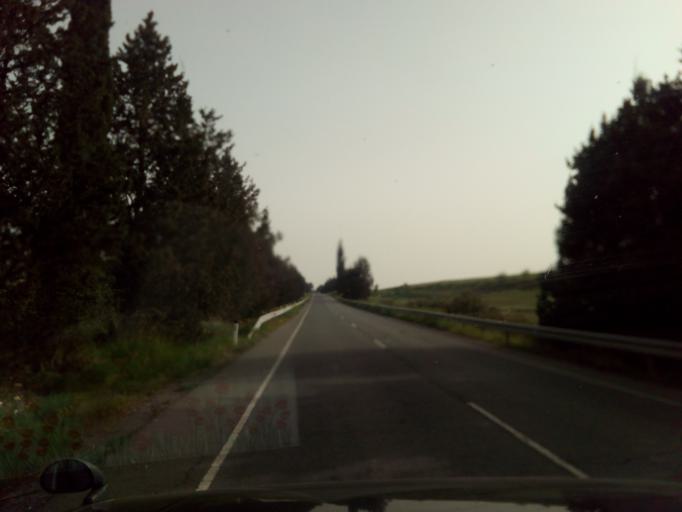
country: CY
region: Lefkosia
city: Lympia
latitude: 35.0221
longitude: 33.4945
